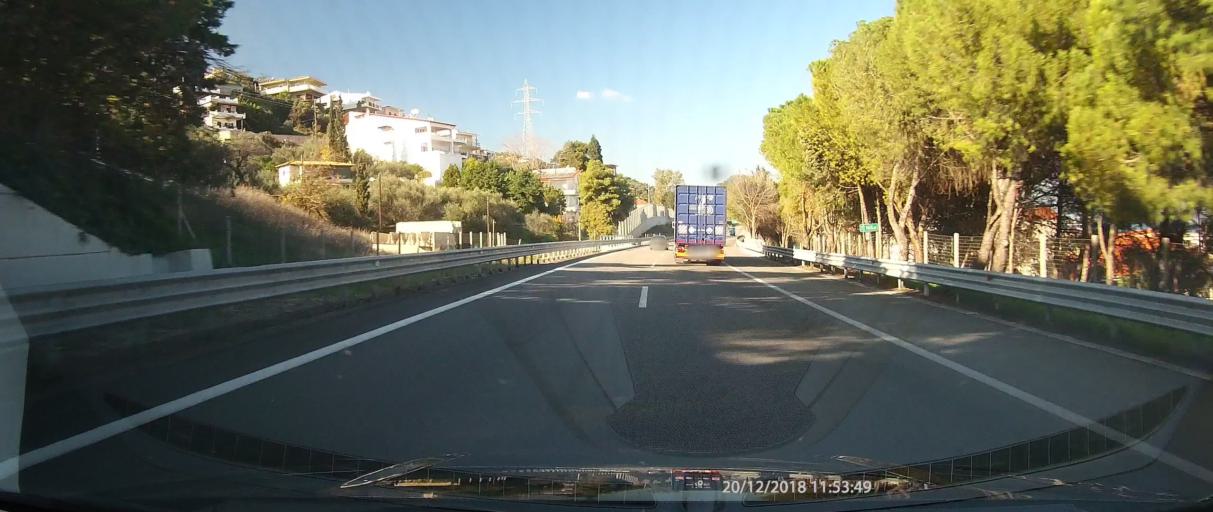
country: GR
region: West Greece
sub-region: Nomos Achaias
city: Aiyira
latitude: 38.1472
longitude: 22.3547
